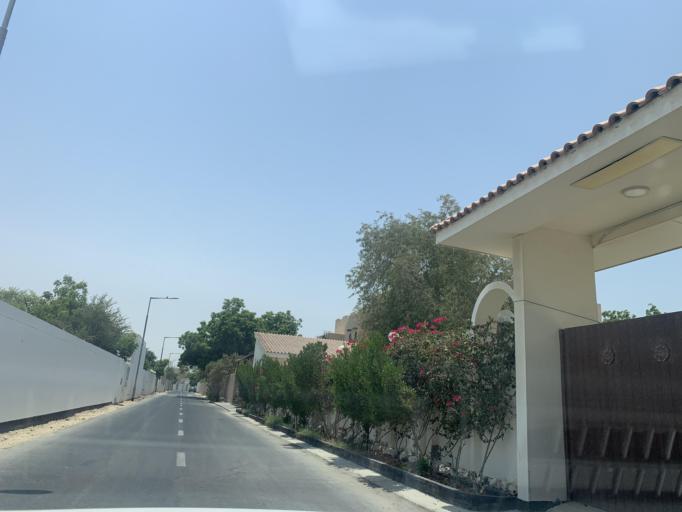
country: BH
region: Manama
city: Jidd Hafs
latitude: 26.2097
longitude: 50.4773
